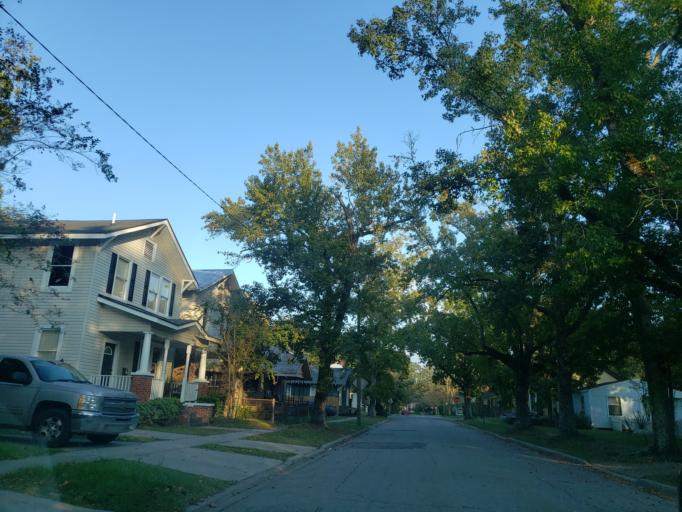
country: US
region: Georgia
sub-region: Chatham County
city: Savannah
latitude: 32.0554
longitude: -81.0864
